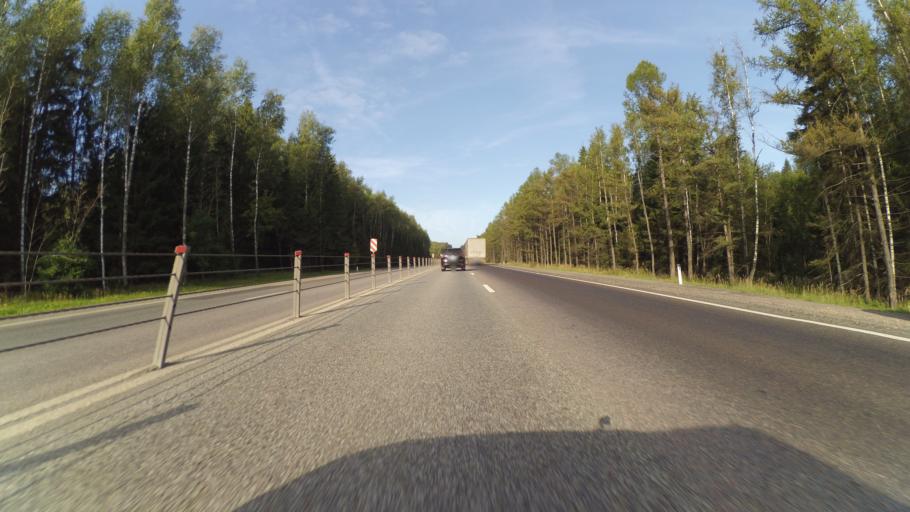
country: RU
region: Moskovskaya
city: Uvarovka
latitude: 55.4636
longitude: 35.7290
